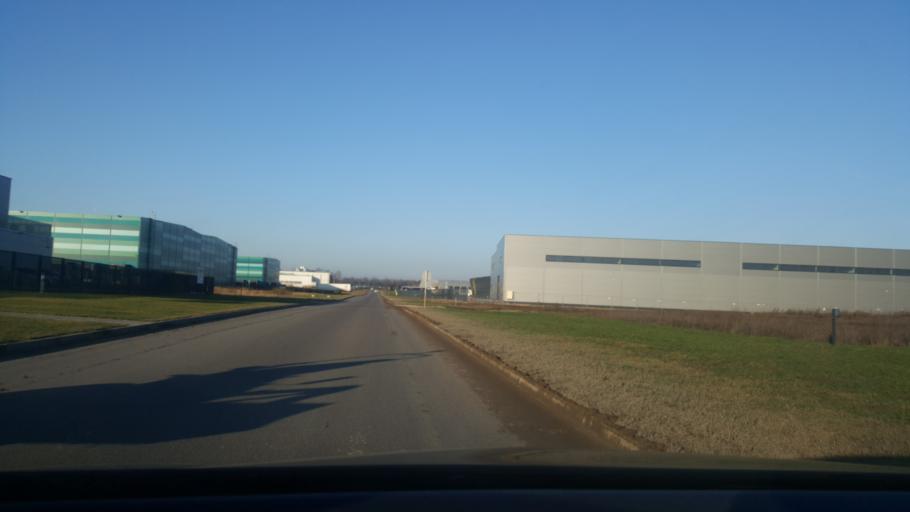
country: LT
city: Ramuciai
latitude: 54.9398
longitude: 24.0163
